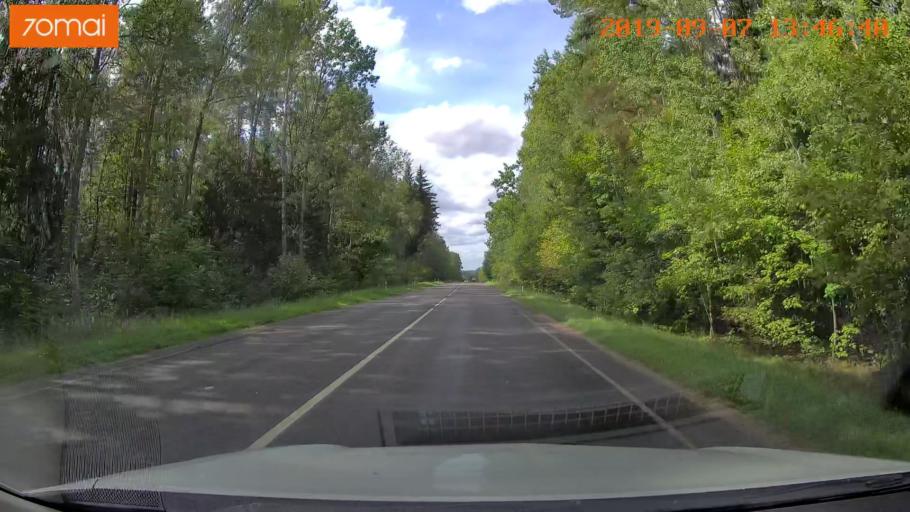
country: LT
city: Baltoji Voke
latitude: 54.5922
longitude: 25.2285
